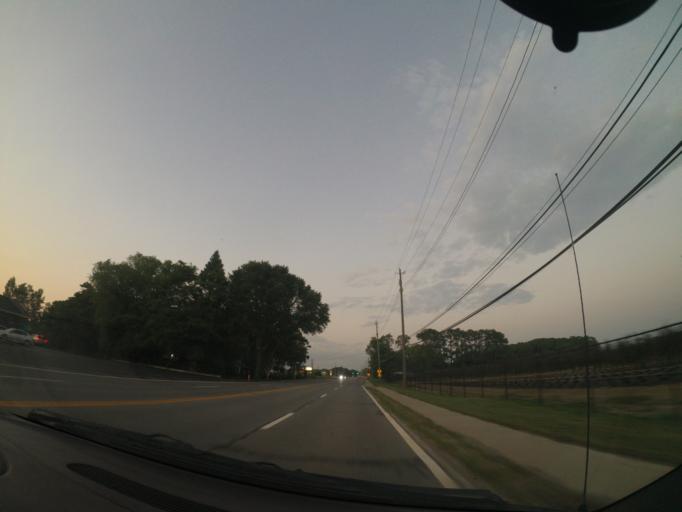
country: US
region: Ohio
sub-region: Lake County
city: North Madison
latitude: 41.7996
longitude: -81.0776
